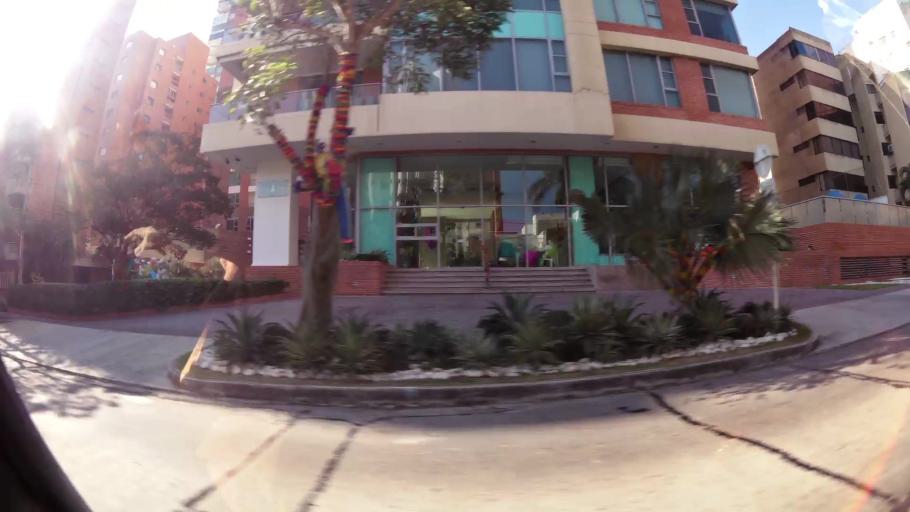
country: CO
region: Atlantico
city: Barranquilla
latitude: 11.0088
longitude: -74.8100
